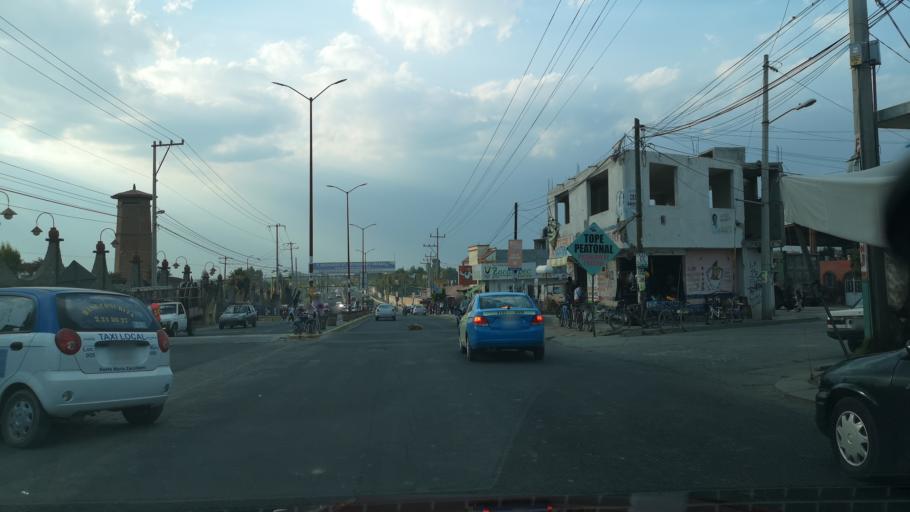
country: MX
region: Puebla
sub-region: Juan C. Bonilla
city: Santa Maria Zacatepec
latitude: 19.1224
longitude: -98.3648
